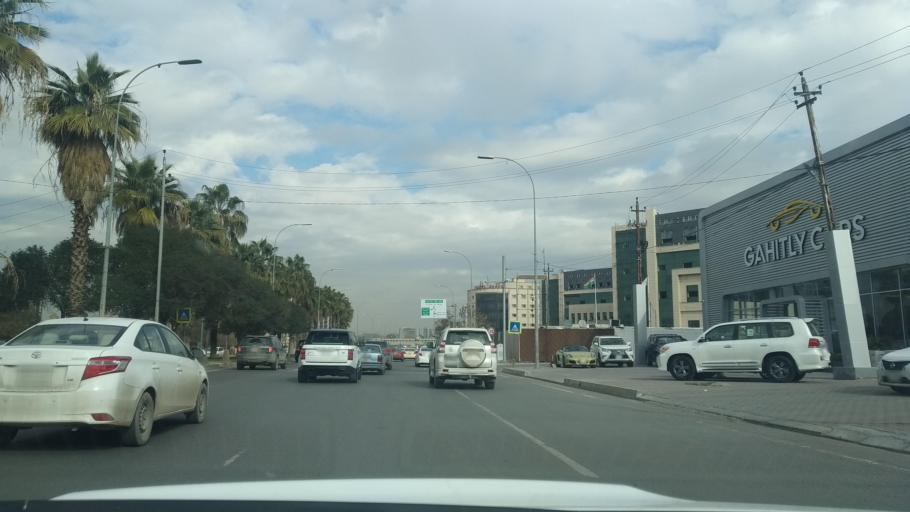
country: IQ
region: Arbil
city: Erbil
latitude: 36.1869
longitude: 43.9938
